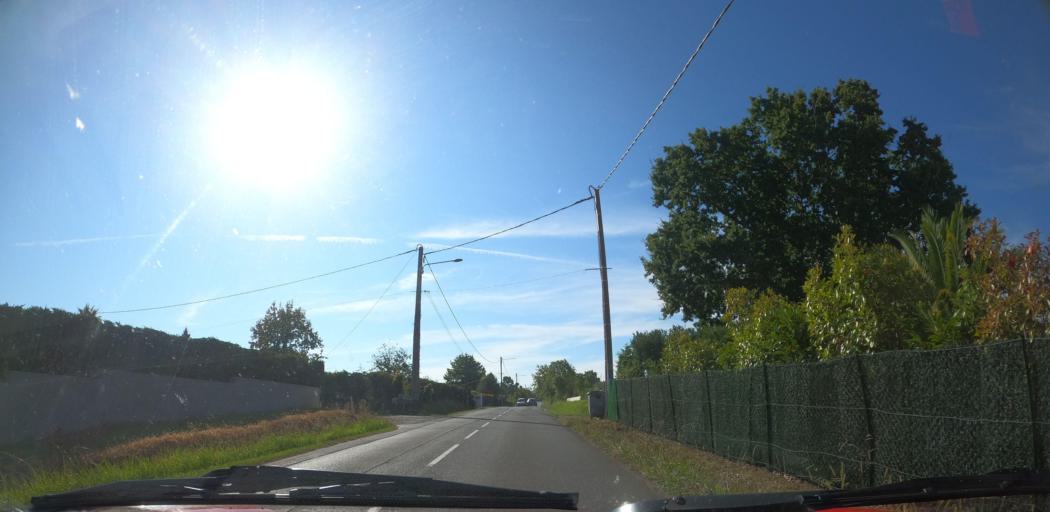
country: FR
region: Aquitaine
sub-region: Departement des Pyrenees-Atlantiques
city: Arbonne
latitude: 43.4098
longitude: -1.5460
